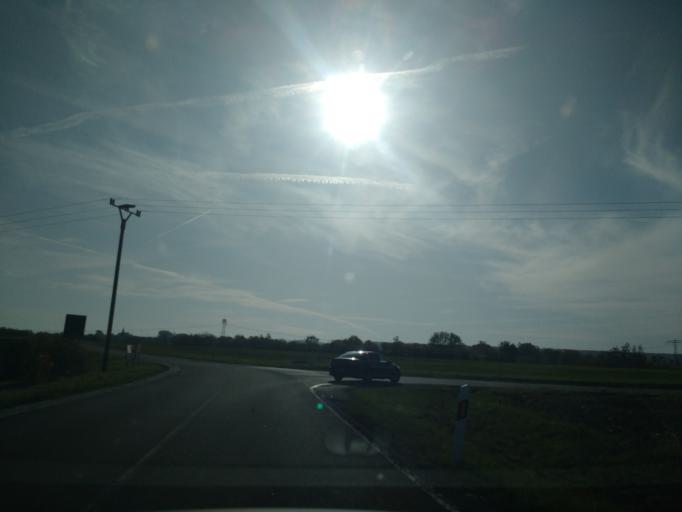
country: DE
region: Thuringia
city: Schonstedt
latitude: 51.0911
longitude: 10.5623
